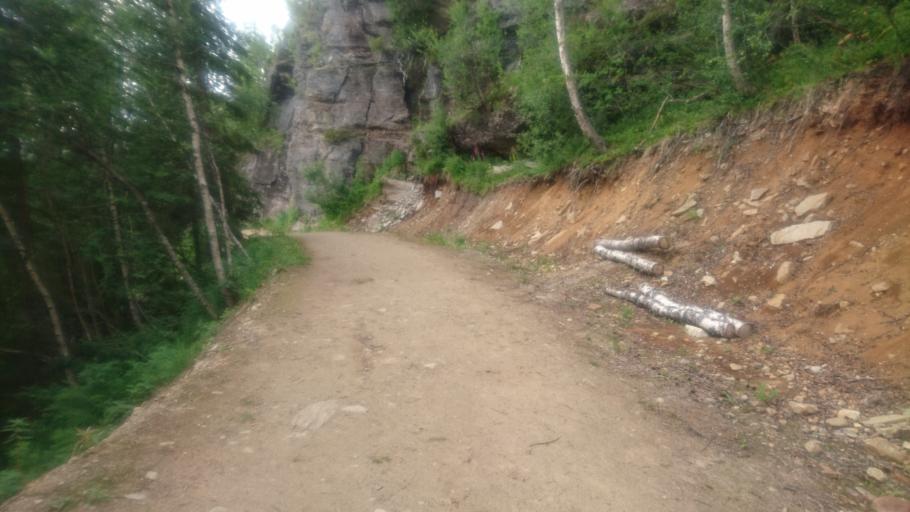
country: NO
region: Nordland
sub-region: Rana
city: Mo i Rana
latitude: 66.4151
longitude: 14.2631
